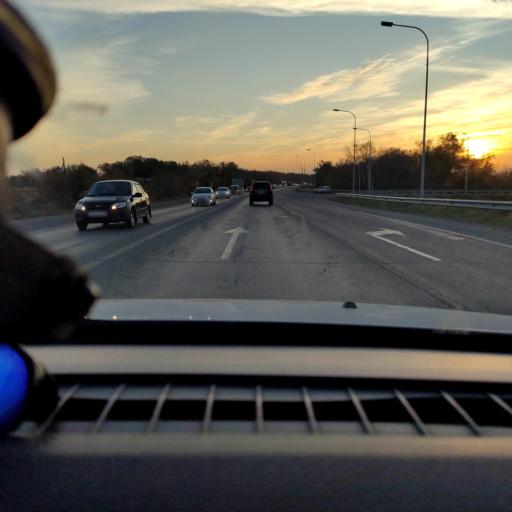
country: RU
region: Samara
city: Samara
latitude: 53.0855
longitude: 50.1418
